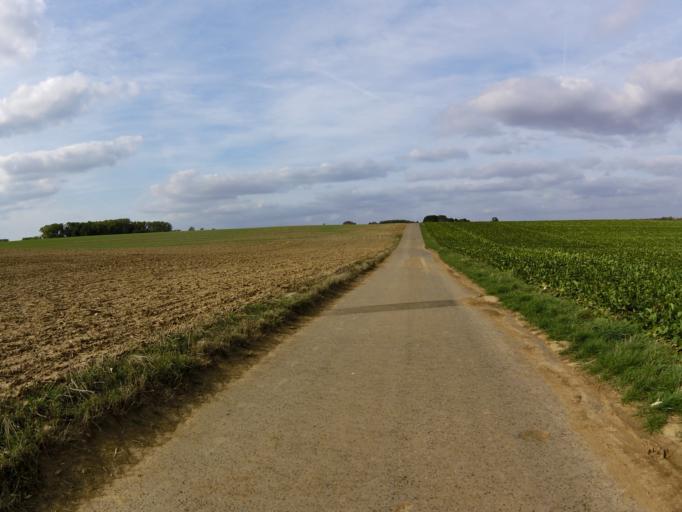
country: DE
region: Bavaria
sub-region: Regierungsbezirk Unterfranken
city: Eibelstadt
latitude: 49.7052
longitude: 9.9602
